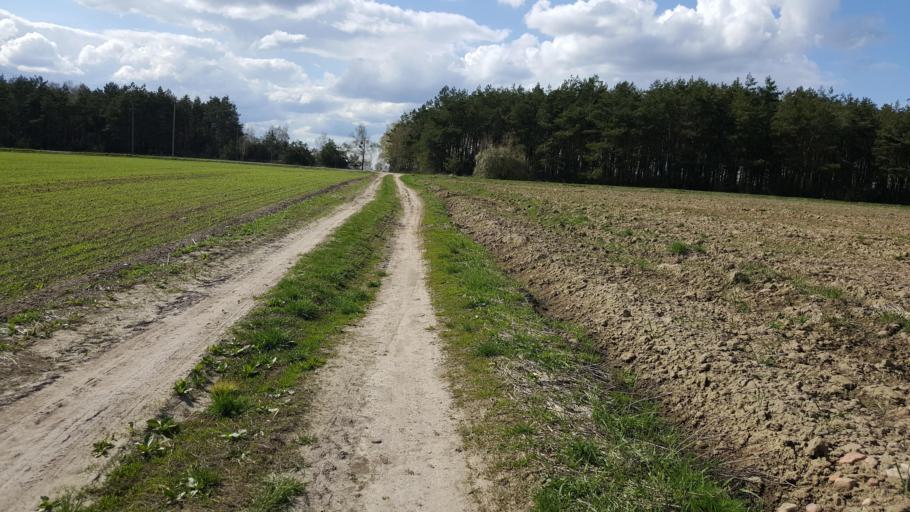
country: BY
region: Brest
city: Kamyanyets
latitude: 52.3911
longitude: 23.6423
